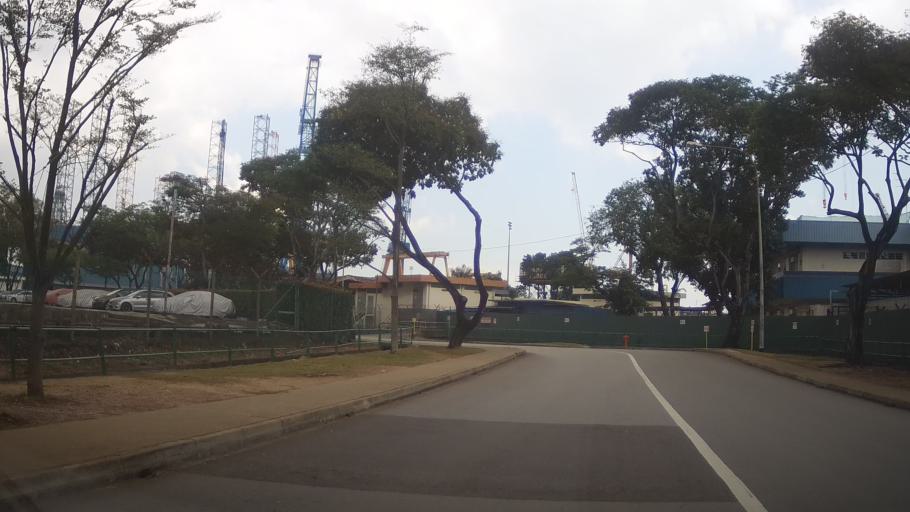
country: SG
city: Singapore
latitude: 1.3011
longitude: 103.6782
